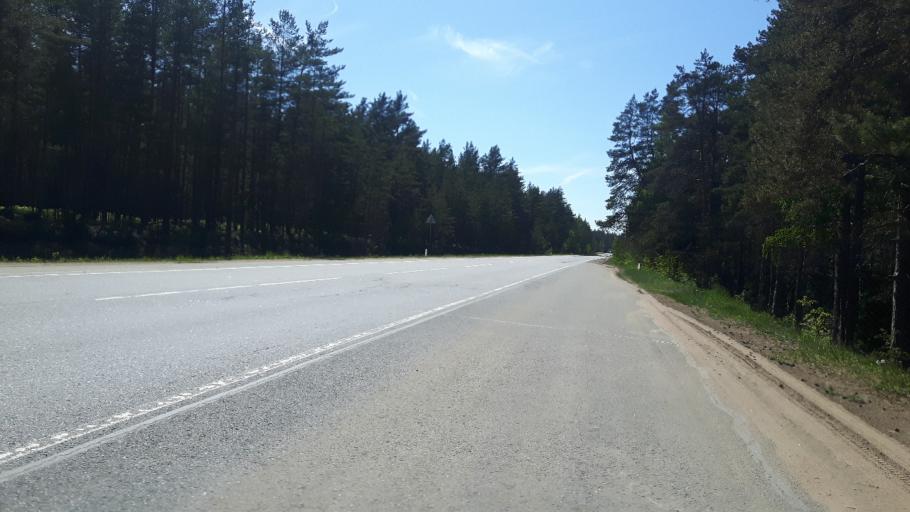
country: RU
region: Leningrad
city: Sista-Palkino
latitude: 59.7688
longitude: 28.8247
